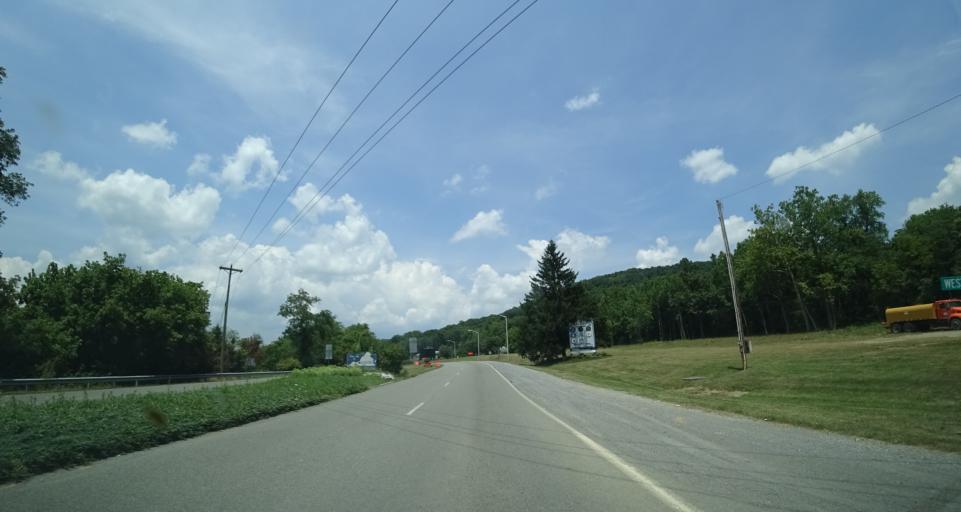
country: US
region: Virginia
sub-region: City of Radford
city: Radford
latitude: 37.0935
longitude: -80.5783
